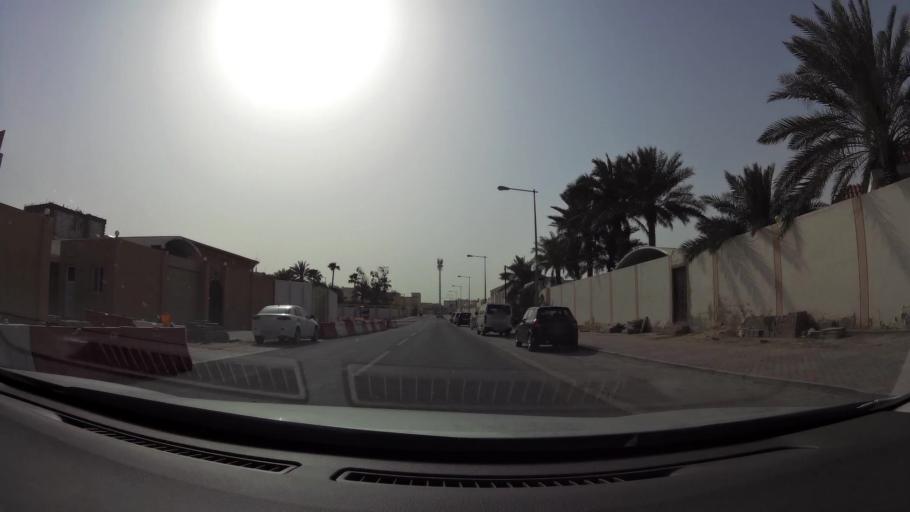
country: QA
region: Baladiyat ar Rayyan
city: Ar Rayyan
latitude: 25.2413
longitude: 51.4381
